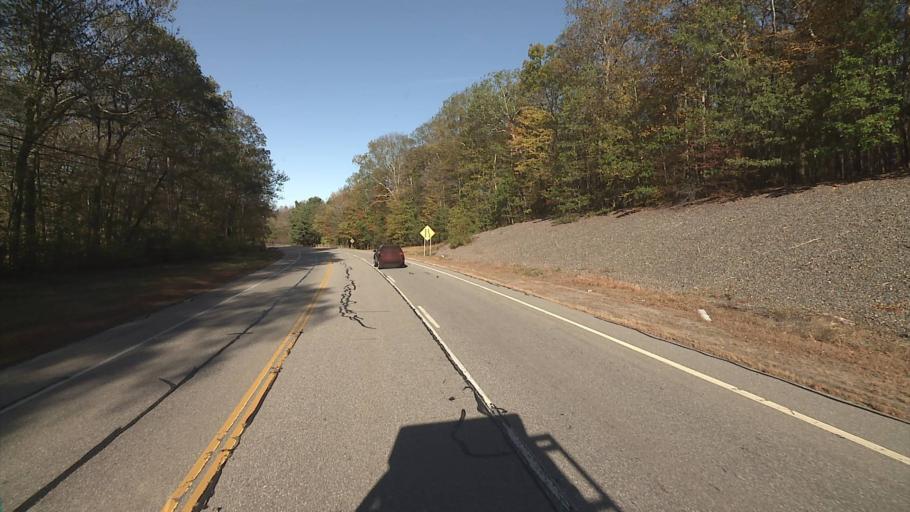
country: US
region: Connecticut
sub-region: Windham County
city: Windham
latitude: 41.7752
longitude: -72.0709
